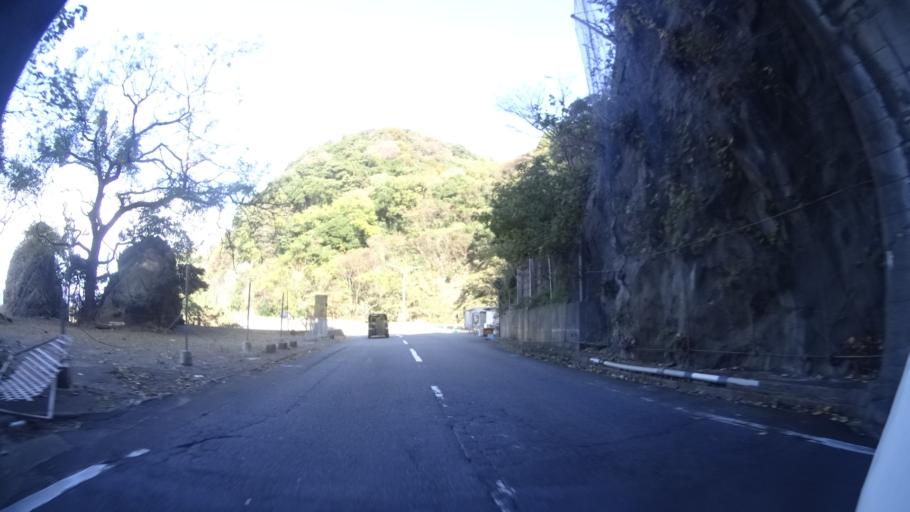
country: JP
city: Asahi
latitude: 35.9598
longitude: 135.9741
